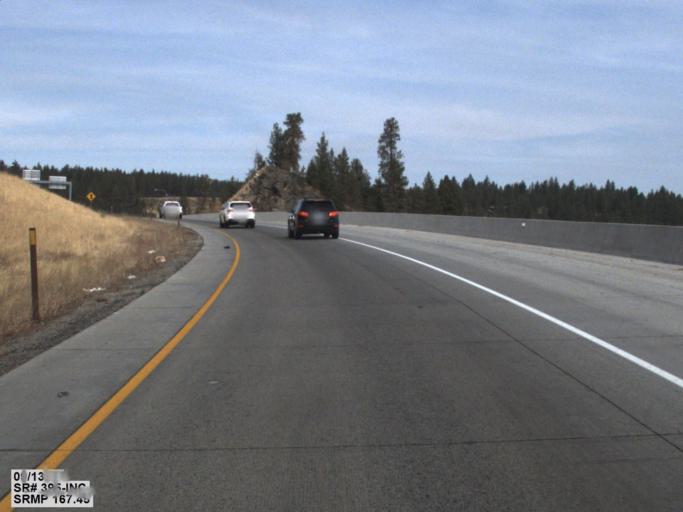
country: US
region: Washington
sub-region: Spokane County
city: Fairwood
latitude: 47.7812
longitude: -117.4028
